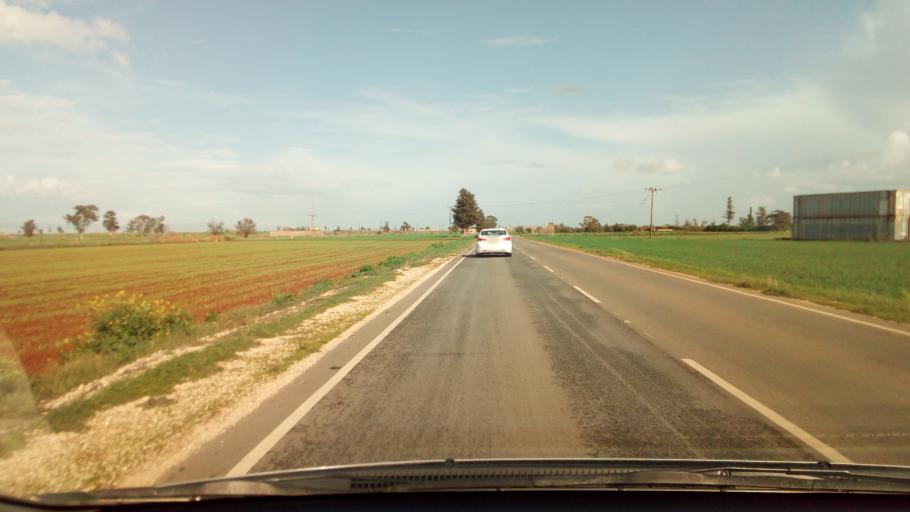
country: CY
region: Ammochostos
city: Achna
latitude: 35.0429
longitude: 33.7685
